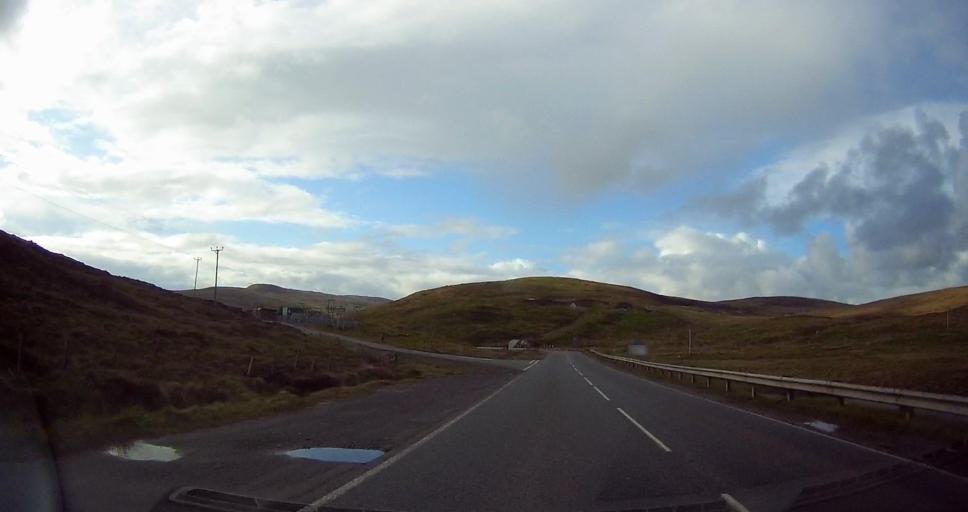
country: GB
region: Scotland
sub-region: Shetland Islands
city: Lerwick
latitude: 60.3479
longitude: -1.2535
